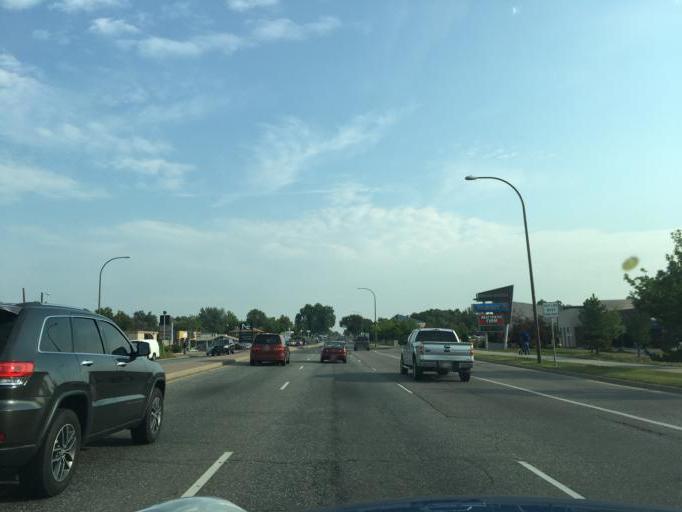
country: US
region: Colorado
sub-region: Jefferson County
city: Edgewater
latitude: 39.7412
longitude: -105.0813
